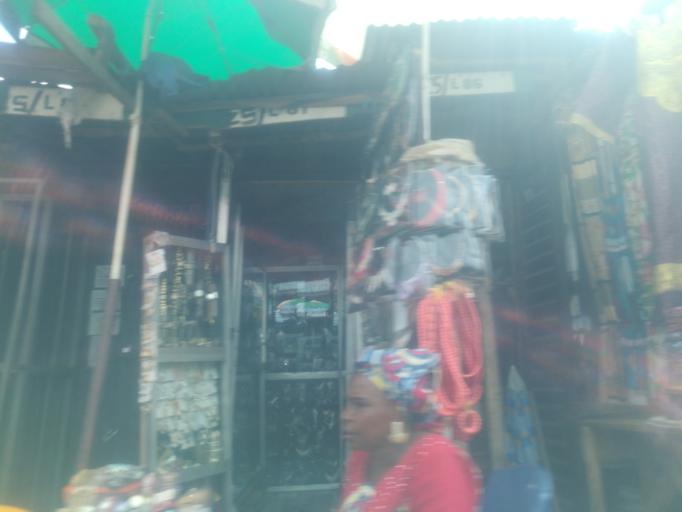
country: NG
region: Oyo
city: Ibadan
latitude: 7.3933
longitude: 3.9576
